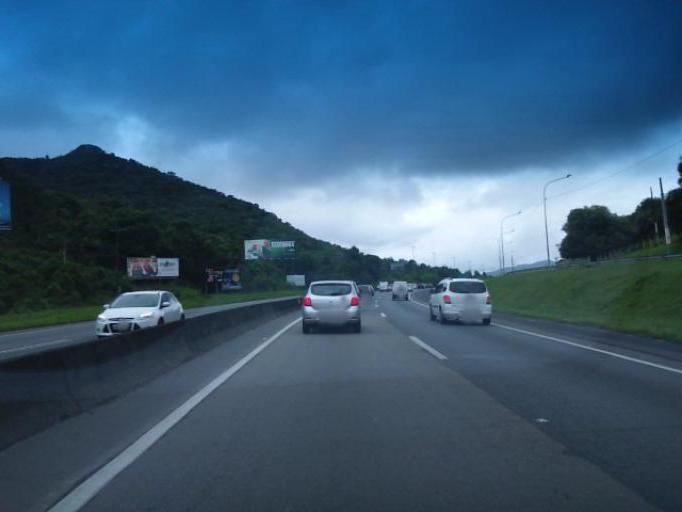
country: BR
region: Santa Catarina
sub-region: Balneario Camboriu
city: Balneario Camboriu
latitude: -26.9847
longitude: -48.6683
